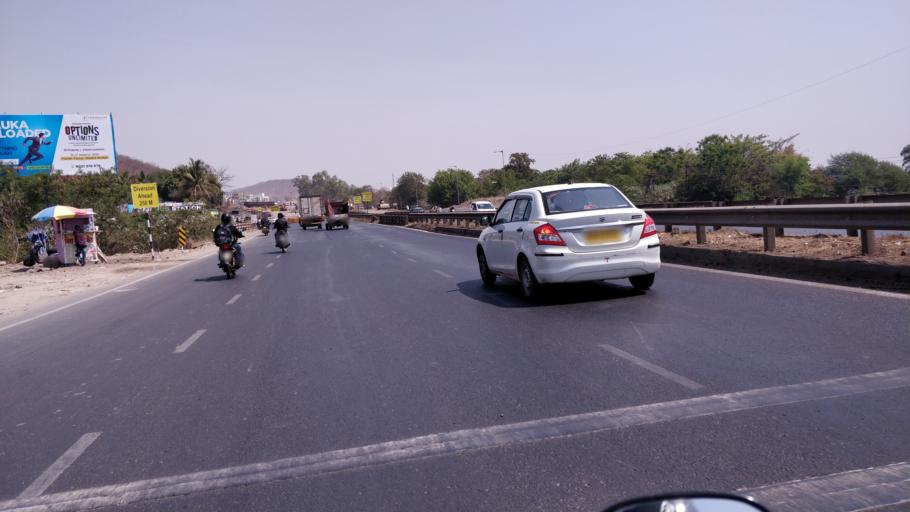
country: IN
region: Maharashtra
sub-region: Pune Division
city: Shivaji Nagar
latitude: 18.5309
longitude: 73.7792
